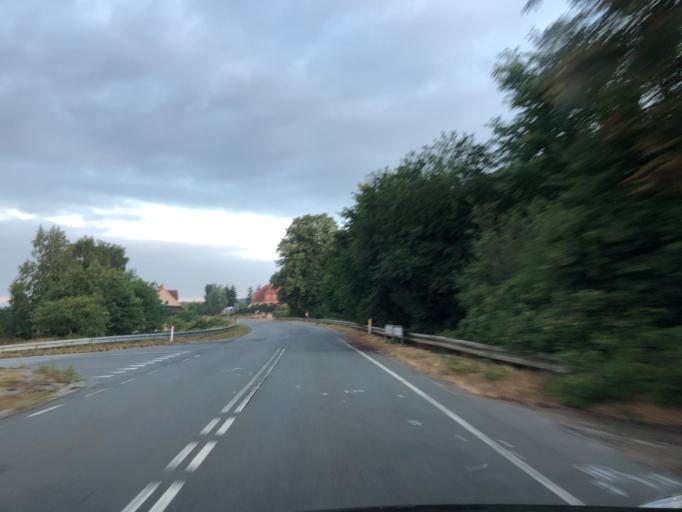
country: DK
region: Zealand
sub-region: Soro Kommune
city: Dianalund
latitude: 55.5047
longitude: 11.5300
